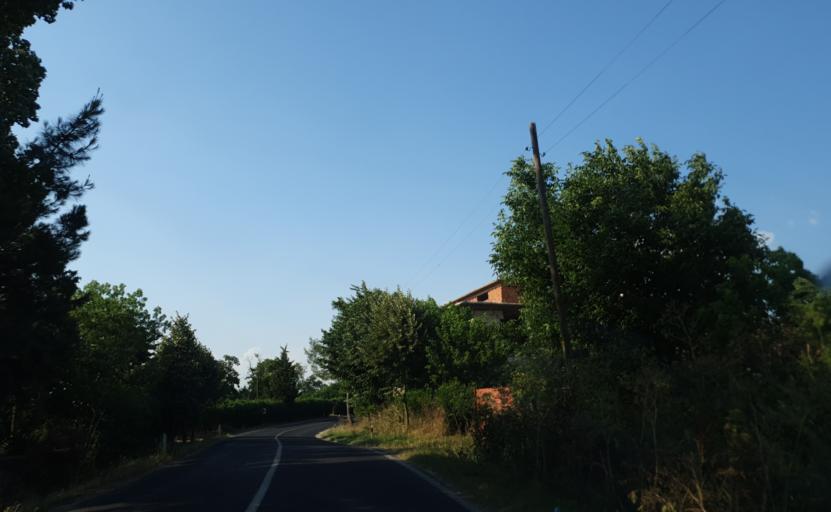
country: TR
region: Tekirdag
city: Muratli
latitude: 41.1995
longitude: 27.4703
